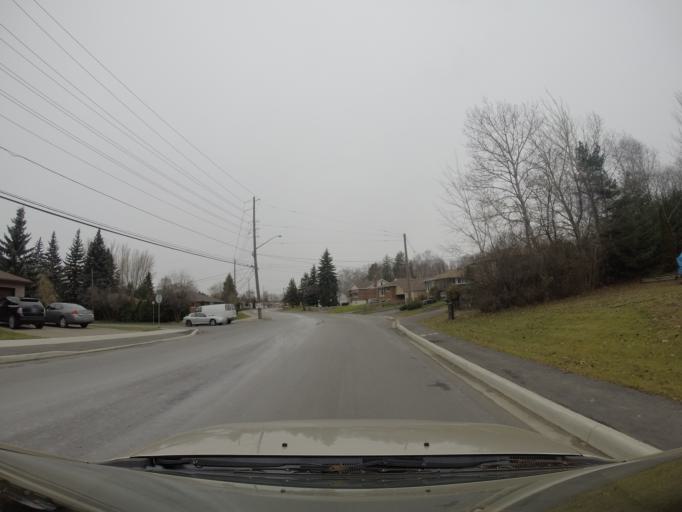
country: CA
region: Ontario
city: Greater Sudbury
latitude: 46.4601
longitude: -81.0188
